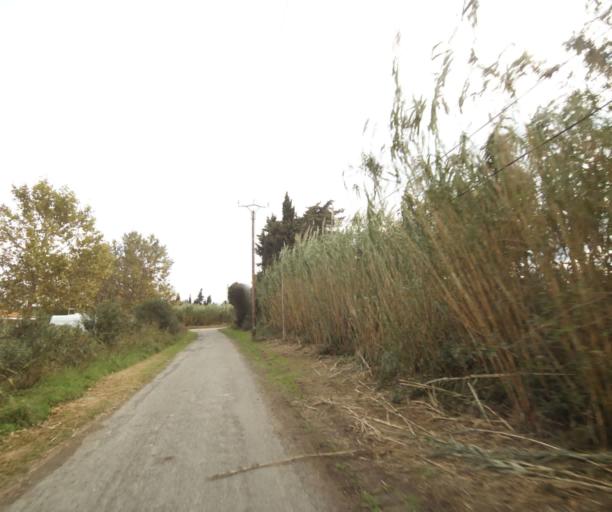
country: FR
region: Languedoc-Roussillon
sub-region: Departement des Pyrenees-Orientales
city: Latour-Bas-Elne
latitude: 42.5839
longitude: 3.0297
